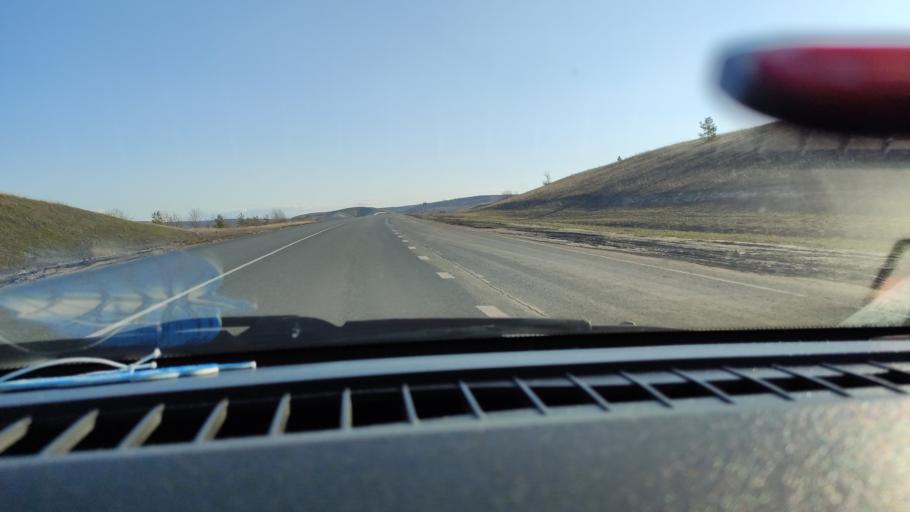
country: RU
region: Saratov
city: Alekseyevka
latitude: 52.3559
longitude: 47.9460
